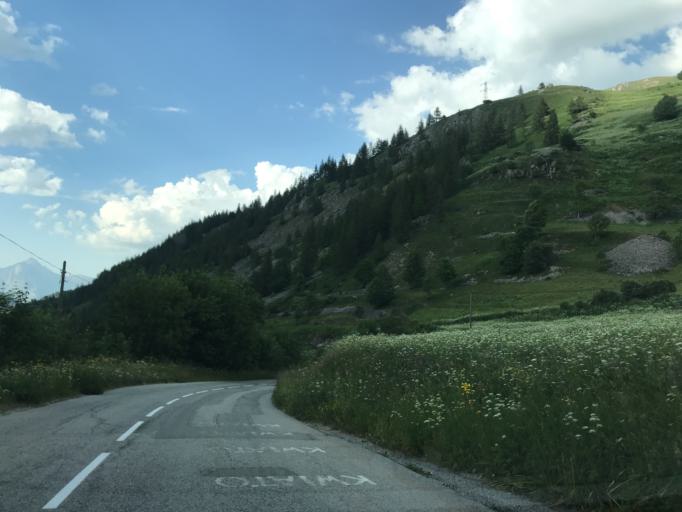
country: FR
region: Rhone-Alpes
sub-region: Departement de la Savoie
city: Valloire
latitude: 45.1242
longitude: 6.4179
